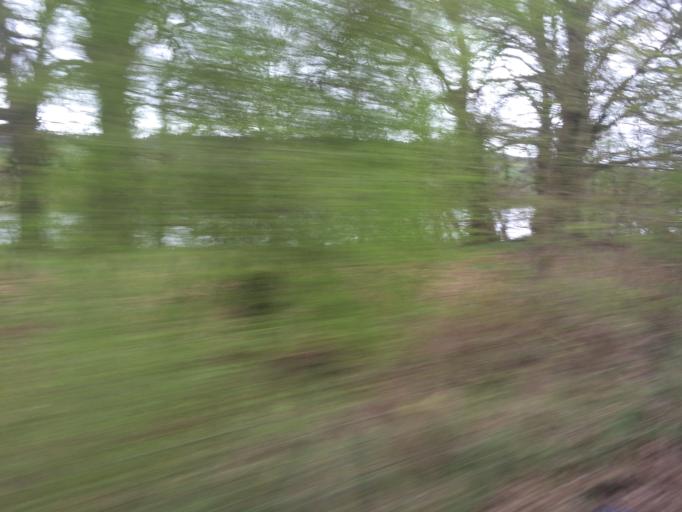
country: GB
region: Scotland
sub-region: Perth and Kinross
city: Scone
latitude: 56.3844
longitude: -3.3907
